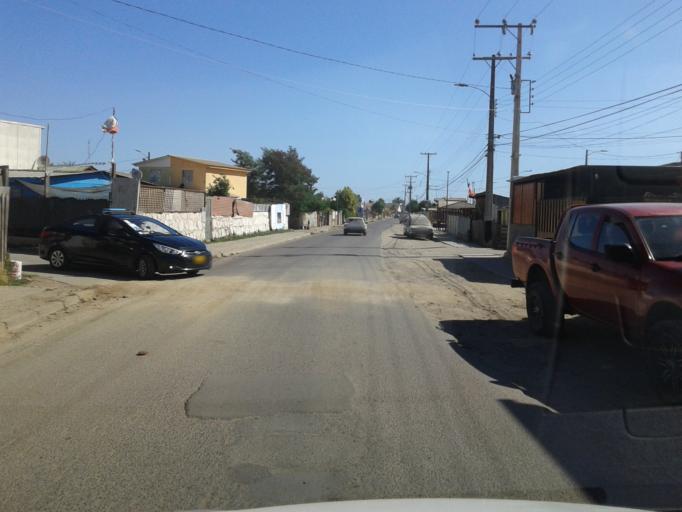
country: CL
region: Valparaiso
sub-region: Provincia de Quillota
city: Quillota
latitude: -32.8757
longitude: -71.2580
